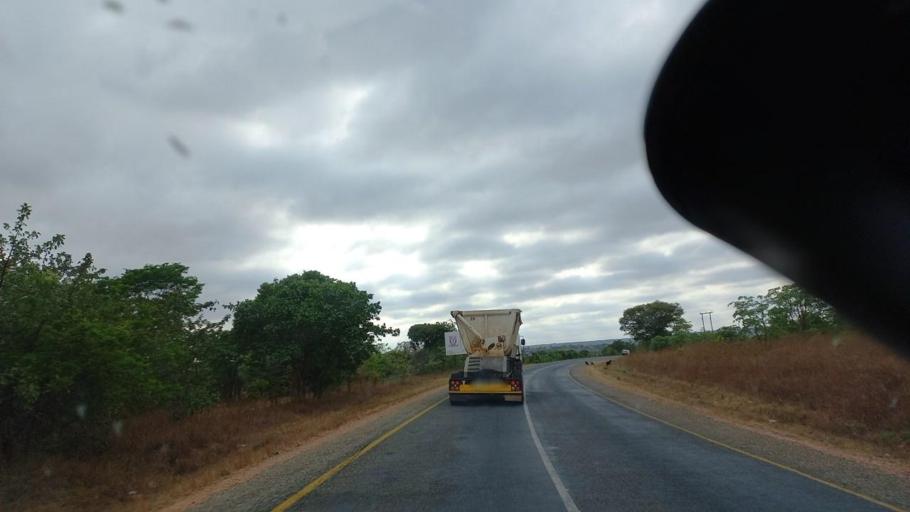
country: ZM
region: Lusaka
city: Chongwe
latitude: -15.2823
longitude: 28.7903
